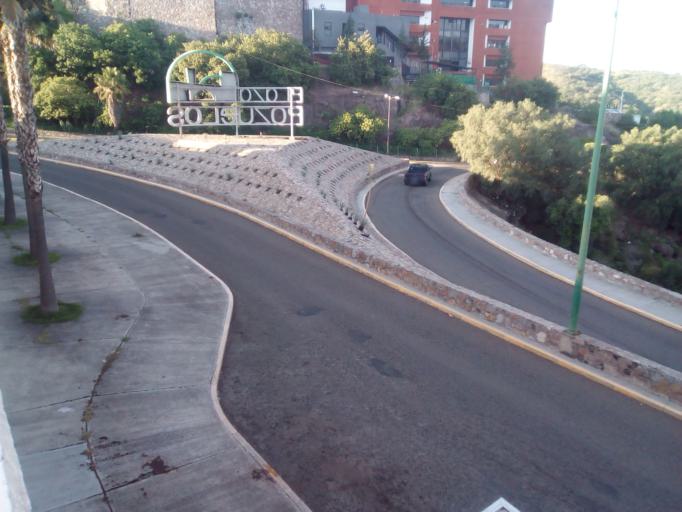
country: MX
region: Guanajuato
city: Guanajuato
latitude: 21.0125
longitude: -101.2617
